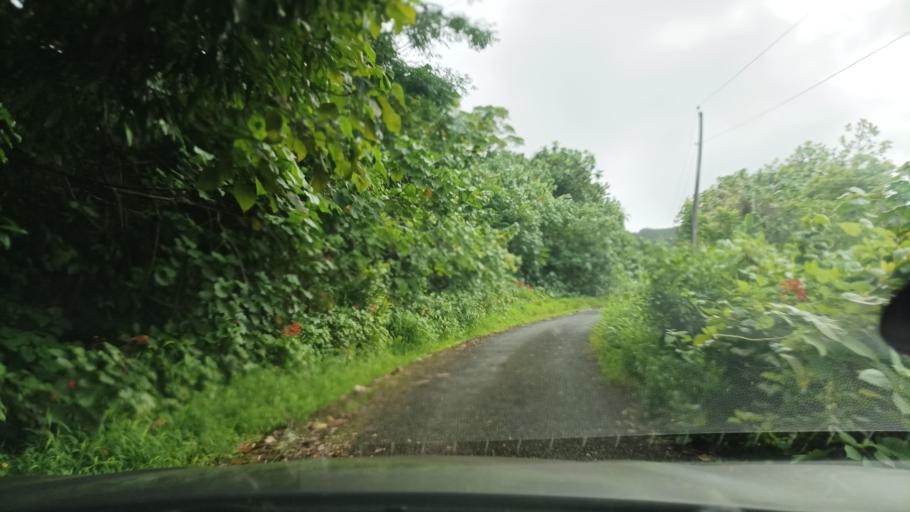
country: FM
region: Pohnpei
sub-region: Kolonia Municipality
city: Kolonia
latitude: 6.9409
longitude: 158.2726
